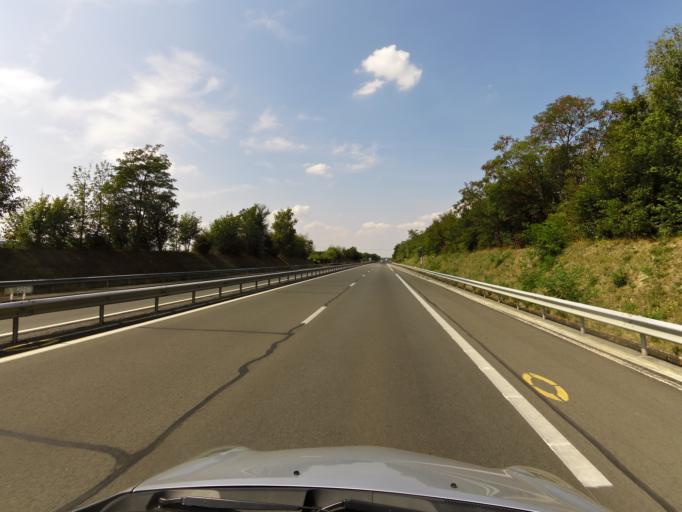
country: FR
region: Picardie
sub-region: Departement de l'Aisne
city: Saint-Erme-Outre-et-Ramecourt
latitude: 49.5317
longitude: 3.8630
